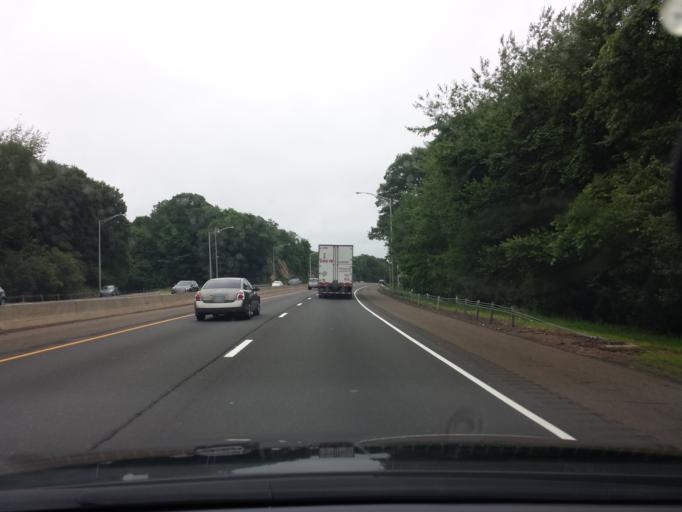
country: US
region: Connecticut
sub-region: New Haven County
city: Branford
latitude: 41.2945
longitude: -72.7892
